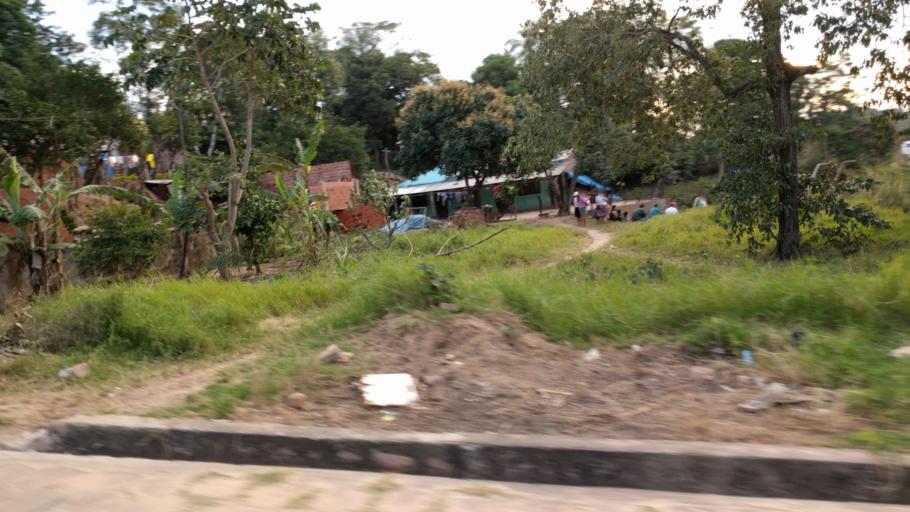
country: BO
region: Santa Cruz
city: Buena Vista
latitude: -17.4555
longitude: -63.6570
